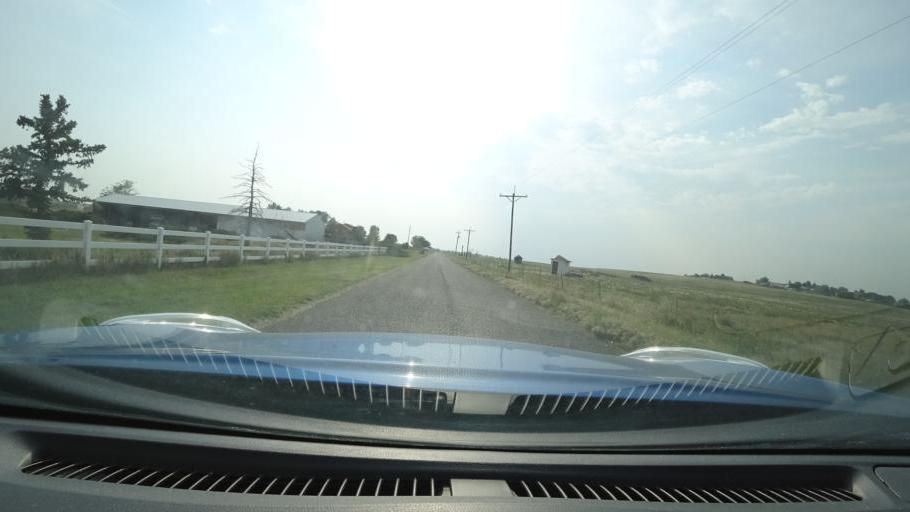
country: US
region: Colorado
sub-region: Adams County
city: Aurora
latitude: 39.7257
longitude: -104.7375
